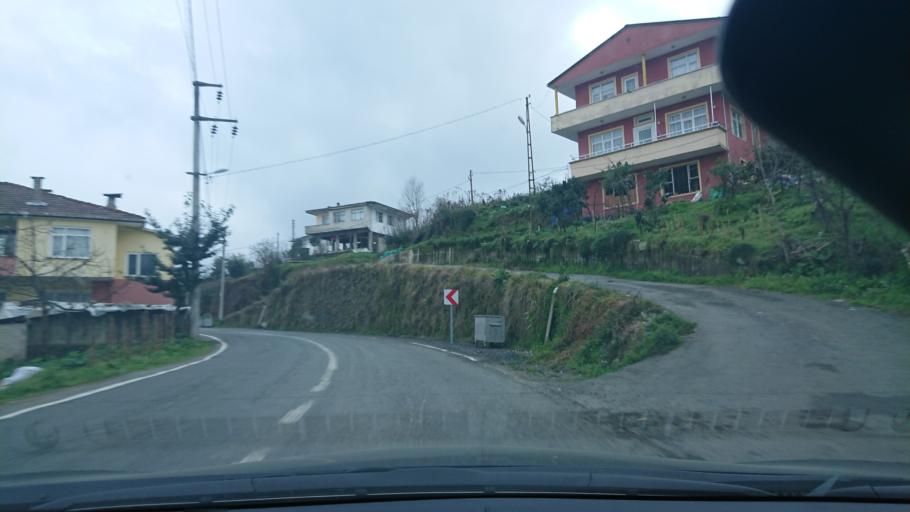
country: TR
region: Rize
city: Rize
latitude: 41.0042
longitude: 40.4866
